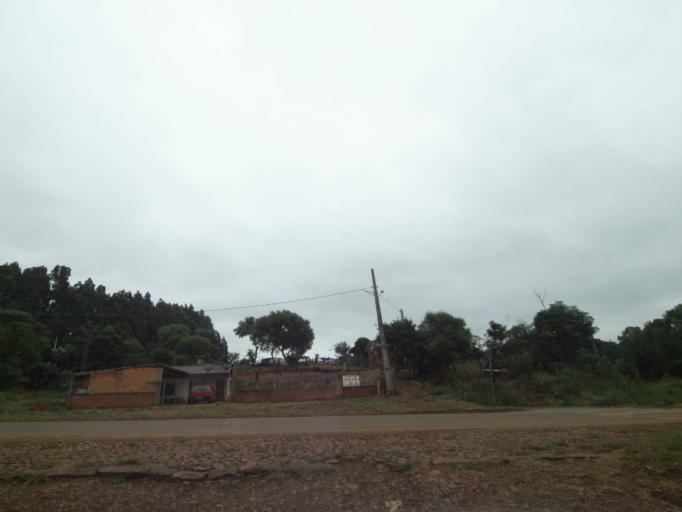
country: BR
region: Parana
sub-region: Pitanga
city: Pitanga
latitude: -24.9291
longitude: -51.8747
